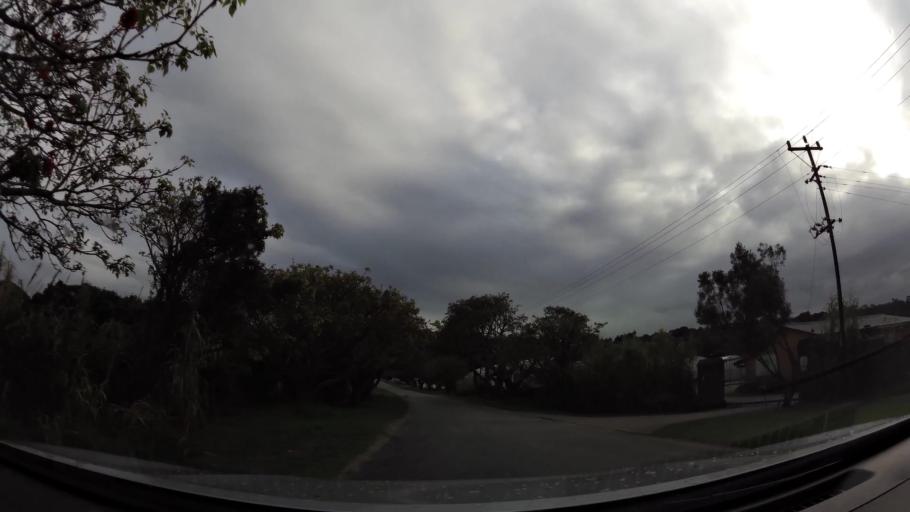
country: ZA
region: Eastern Cape
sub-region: Nelson Mandela Bay Metropolitan Municipality
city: Port Elizabeth
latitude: -34.0129
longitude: 25.4972
